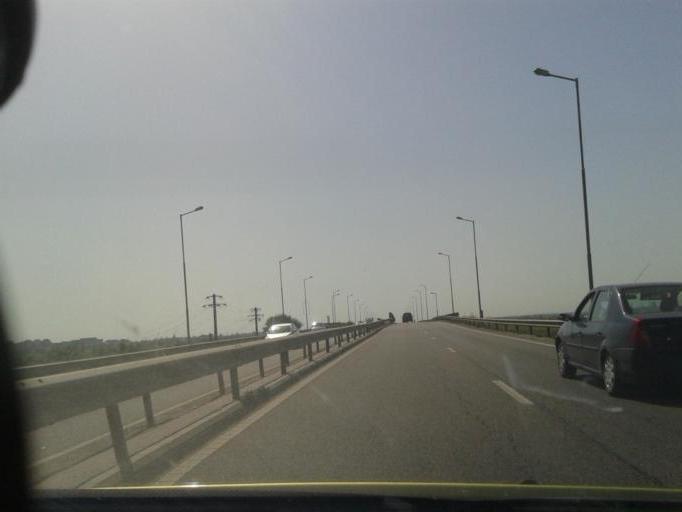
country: RO
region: Prahova
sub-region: Comuna Targsoru Vechi
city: Strejnicu
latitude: 44.9326
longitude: 25.9670
